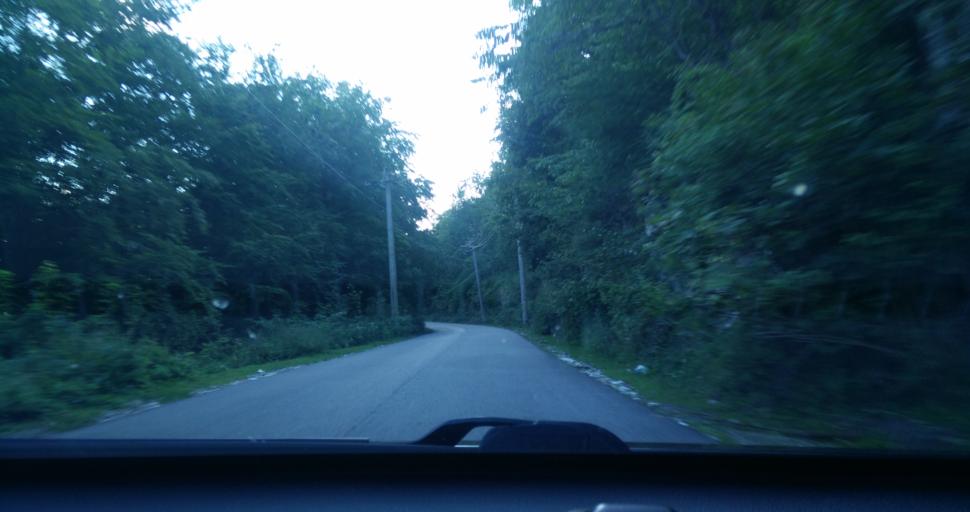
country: RO
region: Bihor
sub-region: Oras Nucet
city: Nucet
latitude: 46.5108
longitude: 22.6226
